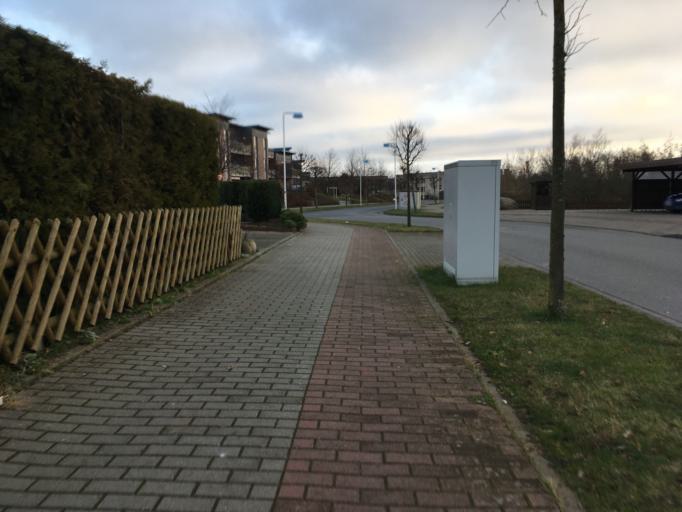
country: DE
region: Mecklenburg-Vorpommern
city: Sassnitz
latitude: 54.5113
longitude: 13.6113
